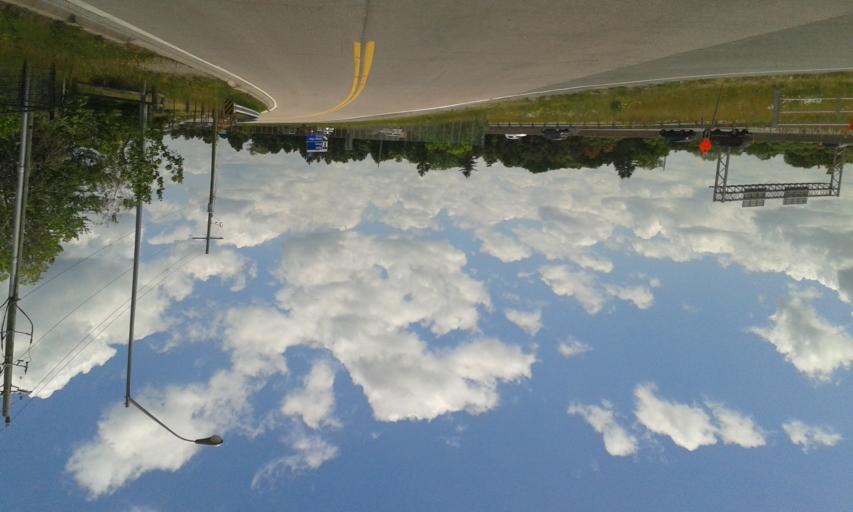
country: CA
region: Ontario
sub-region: Regional Municipality of Niagara
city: St. Catharines
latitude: 43.1818
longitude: -79.3633
